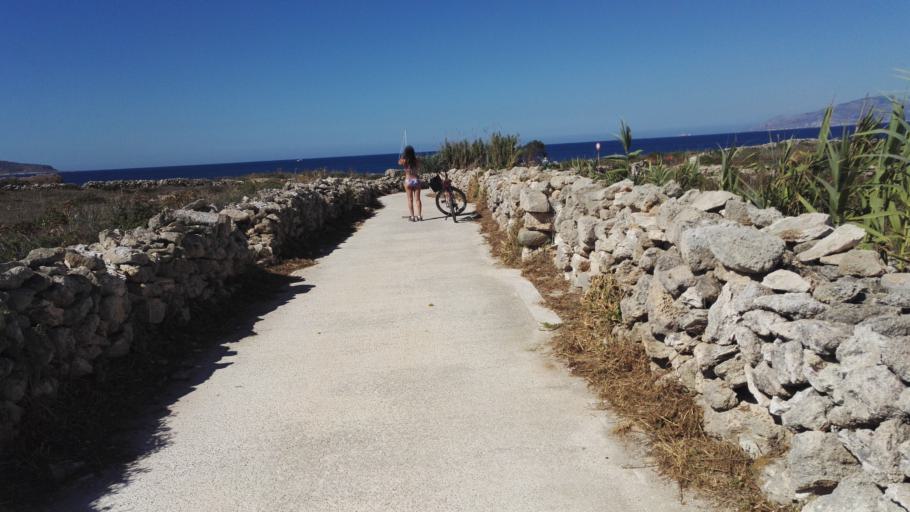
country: IT
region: Sicily
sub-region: Trapani
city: Favignana
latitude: 37.9352
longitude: 12.3441
